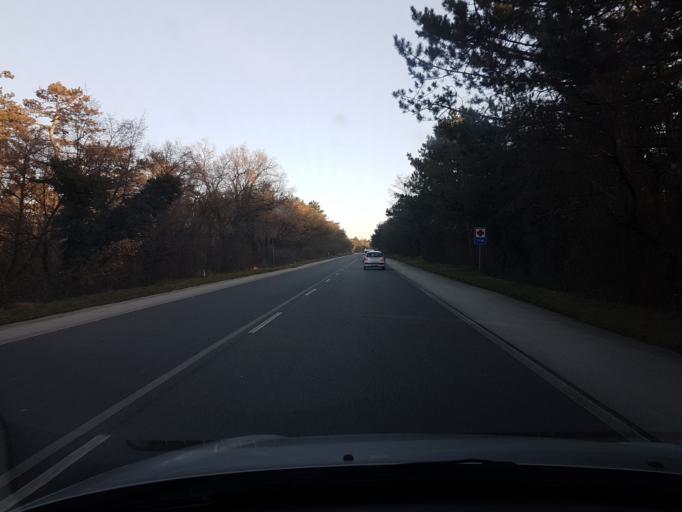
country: IT
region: Friuli Venezia Giulia
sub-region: Provincia di Trieste
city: Prosecco-Contovello
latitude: 45.7006
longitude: 13.7570
